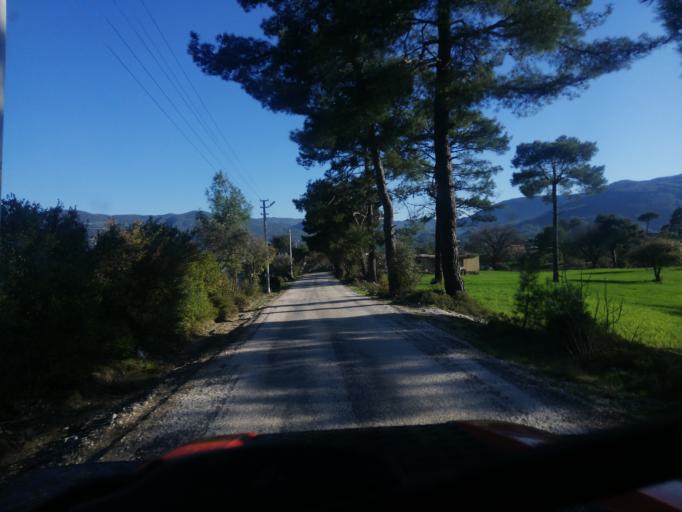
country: TR
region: Antalya
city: Kas
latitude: 36.2937
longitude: 29.7057
